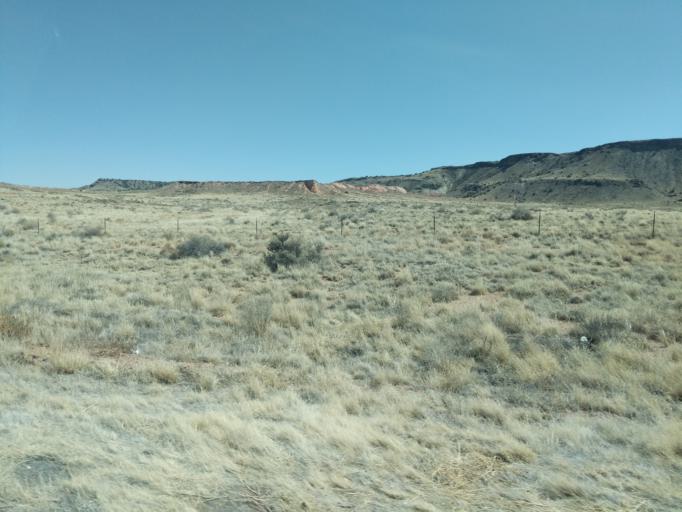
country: US
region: Arizona
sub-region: Navajo County
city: Dilkon
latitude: 35.4446
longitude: -110.0659
